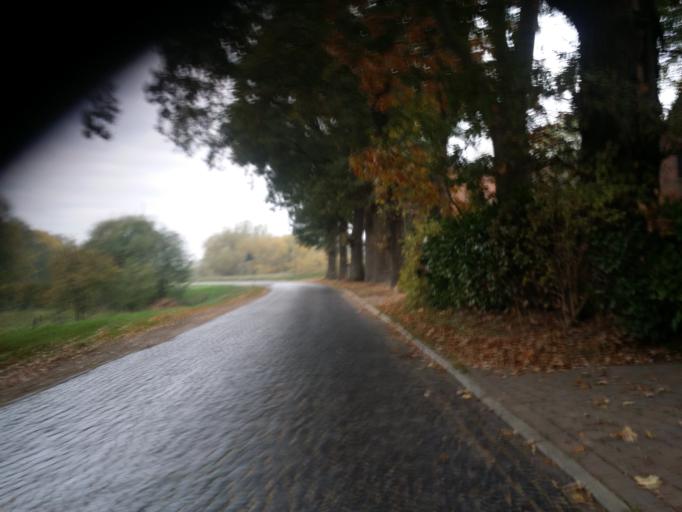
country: DE
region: Lower Saxony
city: Ritterhude
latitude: 53.1652
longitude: 8.7355
